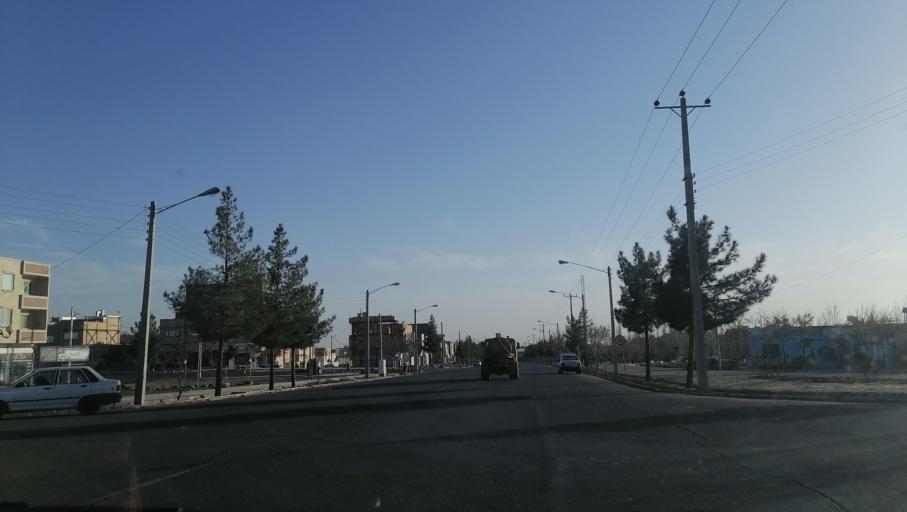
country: IR
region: Razavi Khorasan
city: Sabzevar
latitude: 36.2820
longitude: 57.6751
